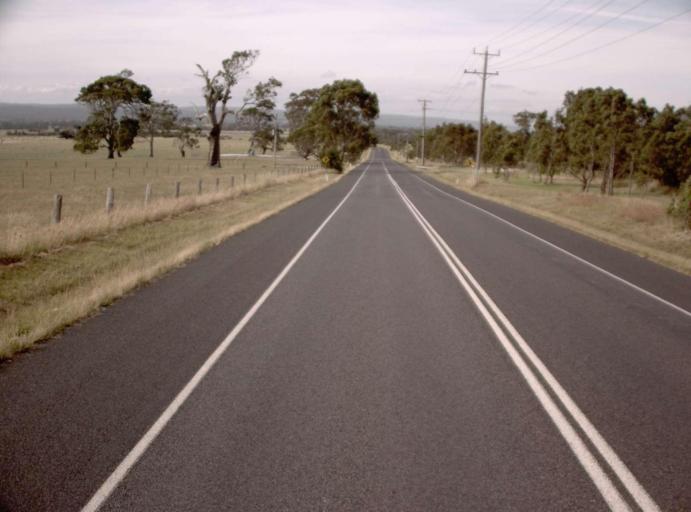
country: AU
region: Victoria
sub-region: Latrobe
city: Traralgon
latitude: -38.1769
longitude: 146.5634
